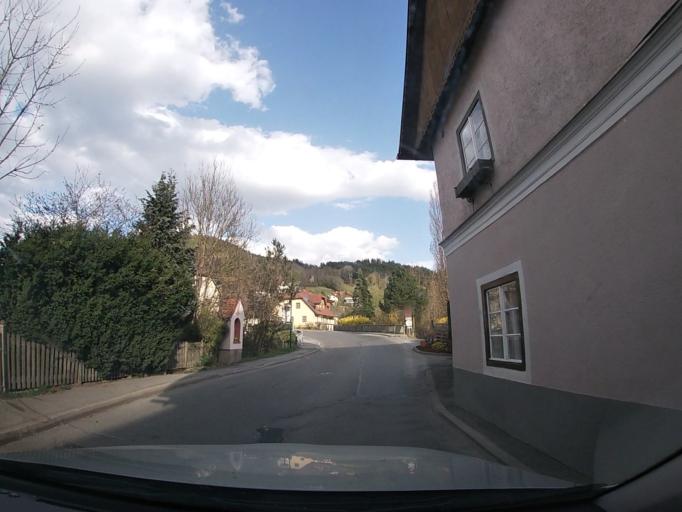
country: AT
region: Styria
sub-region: Politischer Bezirk Murau
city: Teufenbach
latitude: 47.1283
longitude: 14.3596
